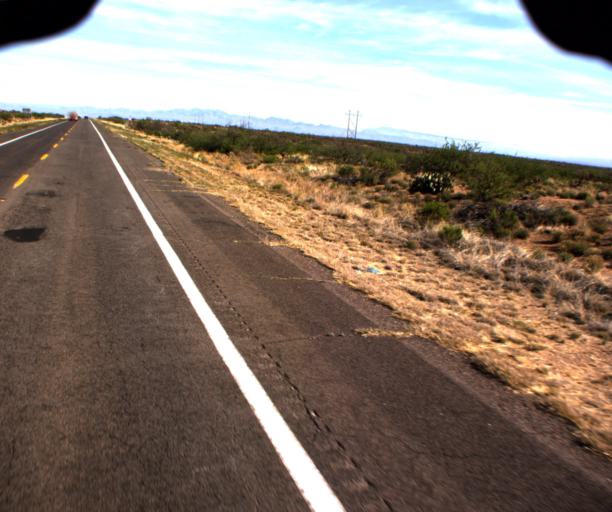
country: US
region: Arizona
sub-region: Graham County
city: Swift Trail Junction
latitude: 32.6200
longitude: -109.6889
